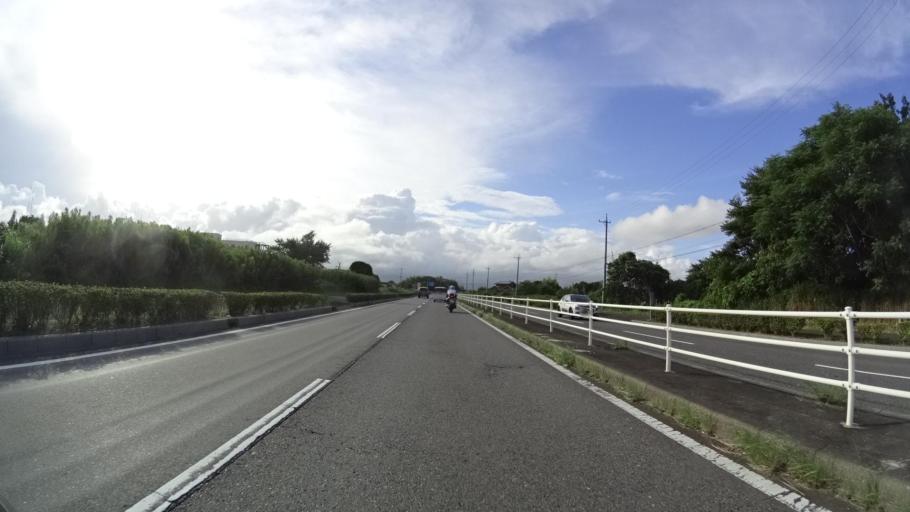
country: JP
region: Mie
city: Kameyama
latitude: 34.8861
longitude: 136.5112
